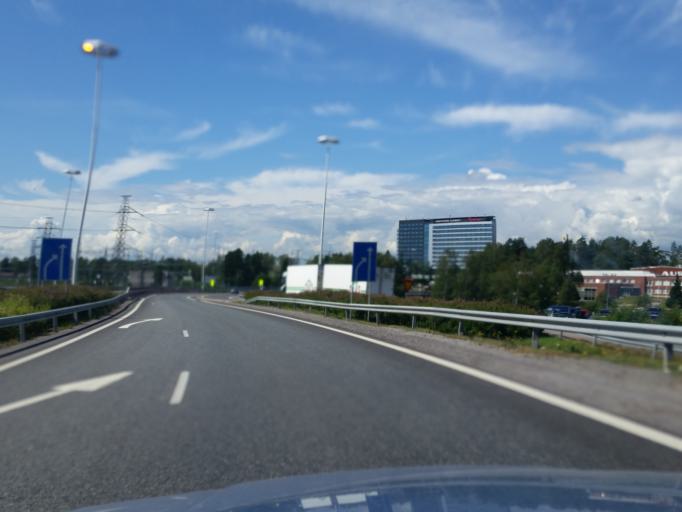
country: FI
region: Uusimaa
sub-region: Helsinki
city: Vantaa
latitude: 60.2897
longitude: 24.9801
